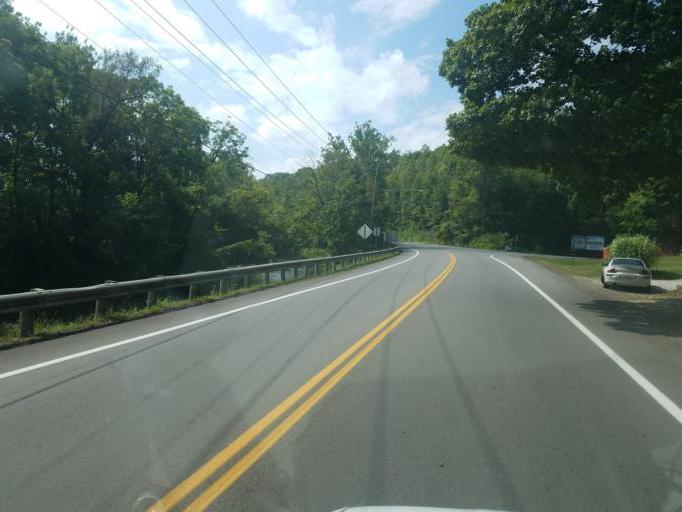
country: US
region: Ohio
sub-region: Sandusky County
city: Bellville
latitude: 40.6255
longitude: -82.5132
